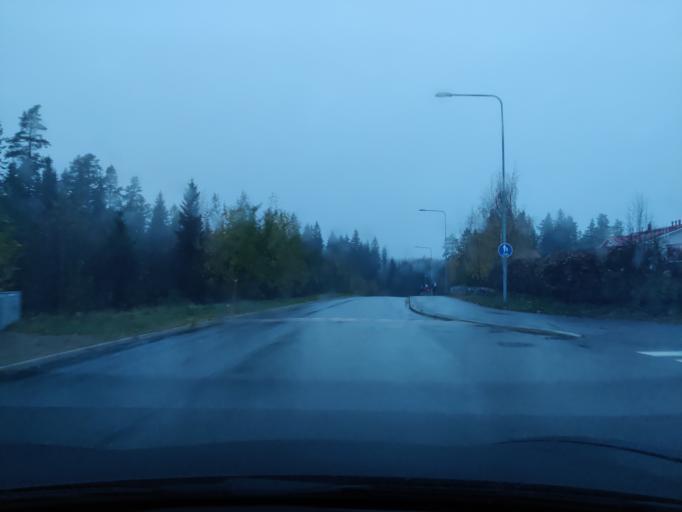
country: FI
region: Northern Savo
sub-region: Kuopio
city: Kuopio
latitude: 62.8288
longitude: 27.7176
